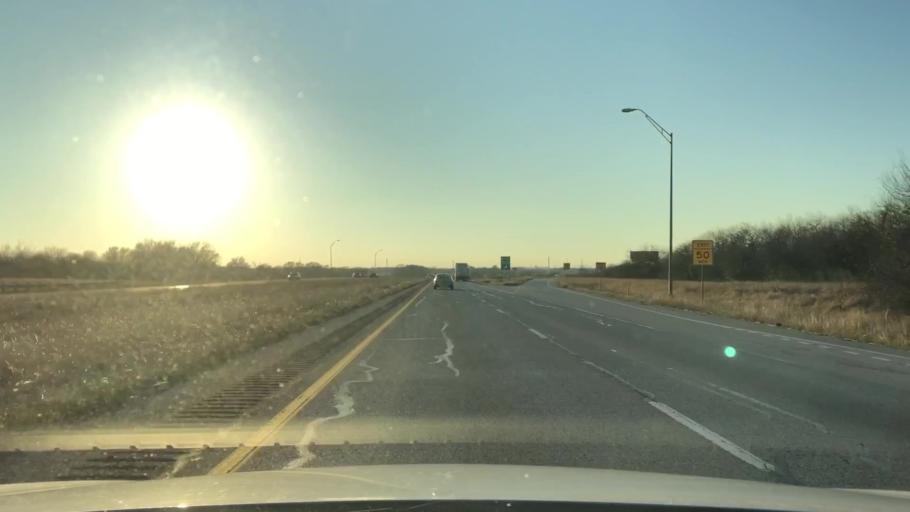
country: US
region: Texas
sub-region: Guadalupe County
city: Seguin
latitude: 29.6011
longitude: -97.9111
